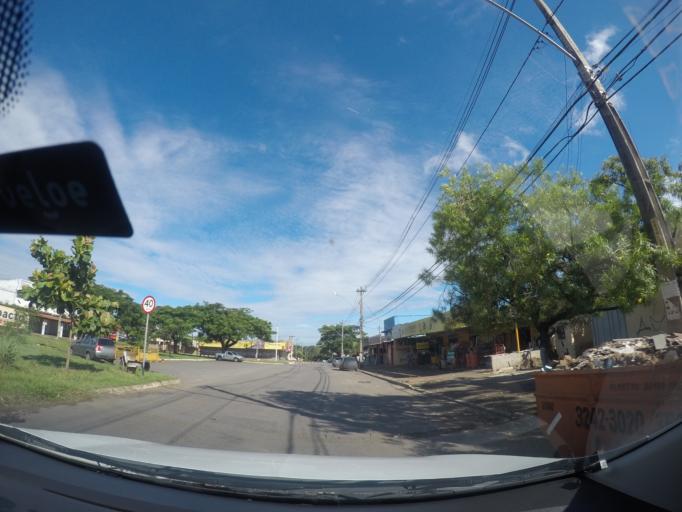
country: BR
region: Goias
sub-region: Goiania
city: Goiania
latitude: -16.6646
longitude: -49.2140
